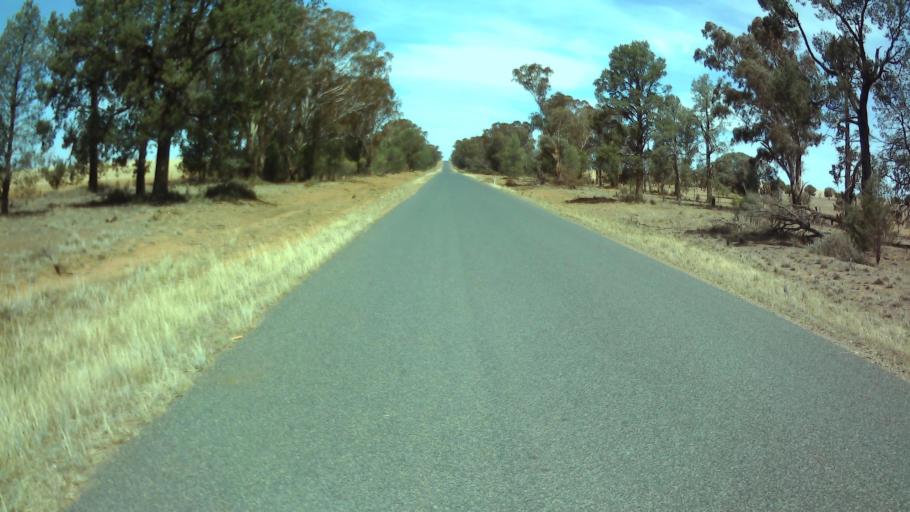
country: AU
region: New South Wales
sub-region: Weddin
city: Grenfell
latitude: -33.8949
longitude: 147.7485
